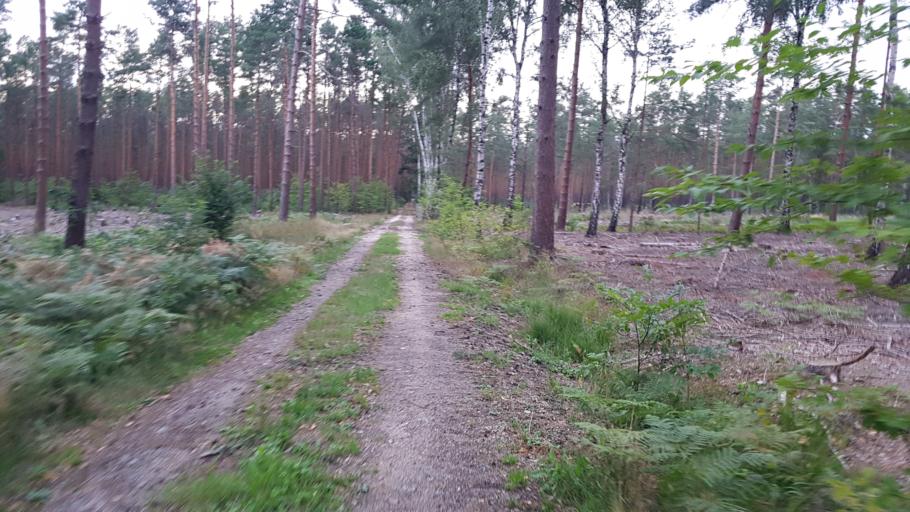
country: DE
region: Brandenburg
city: Schonborn
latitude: 51.5664
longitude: 13.4755
